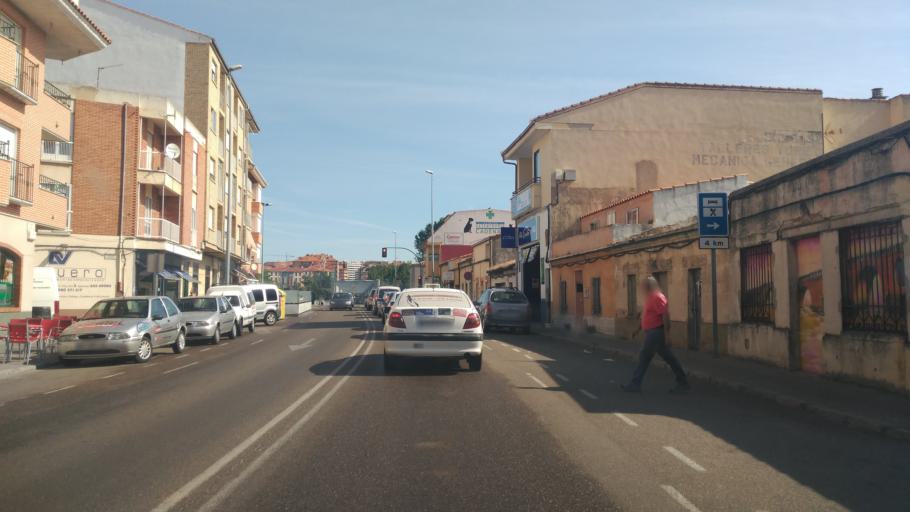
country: ES
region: Castille and Leon
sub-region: Provincia de Zamora
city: Zamora
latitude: 41.4975
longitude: -5.7399
